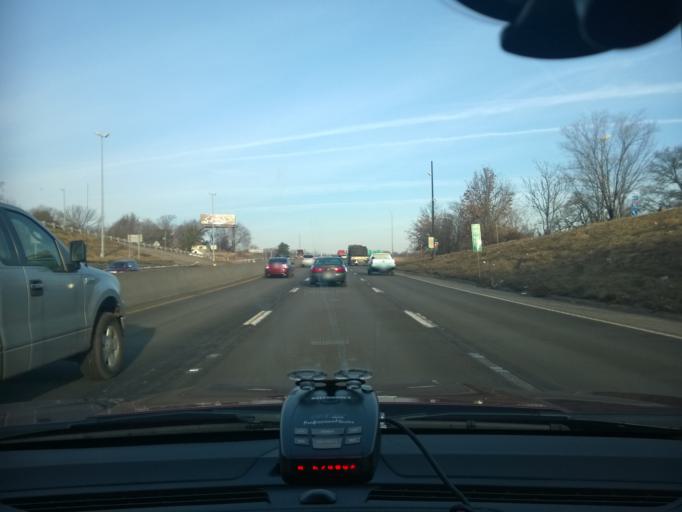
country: US
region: Missouri
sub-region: Saint Louis County
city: Pine Lawn
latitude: 38.7010
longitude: -90.2650
